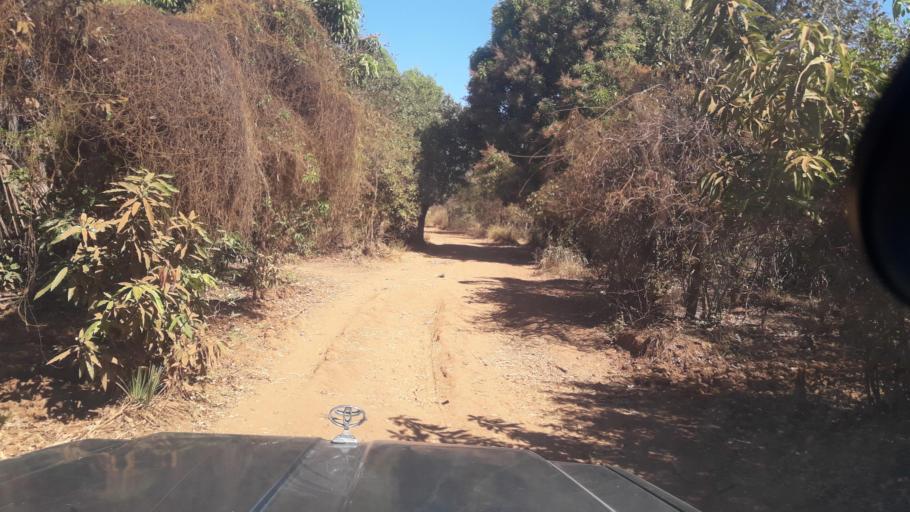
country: MG
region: Boeny
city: Sitampiky
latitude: -16.2355
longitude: 45.6857
